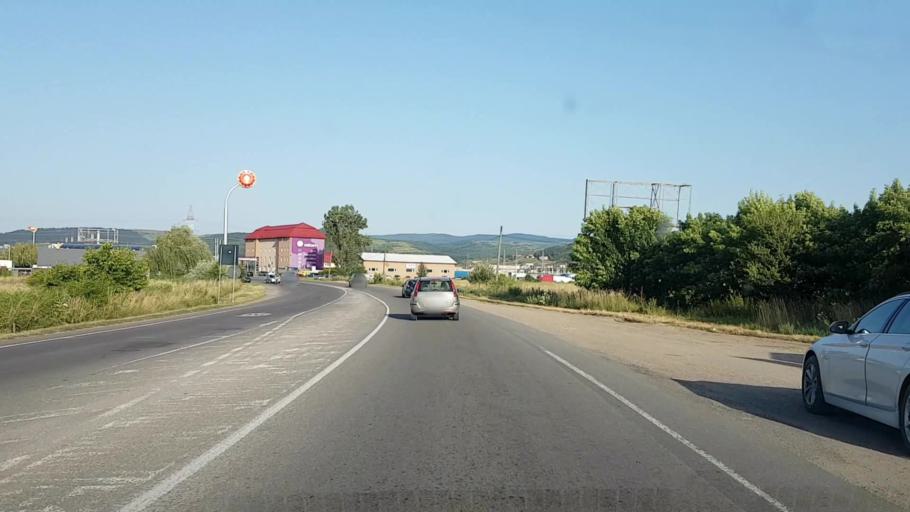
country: RO
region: Cluj
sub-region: Comuna Floresti
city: Luna de Sus
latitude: 46.7450
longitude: 23.4525
